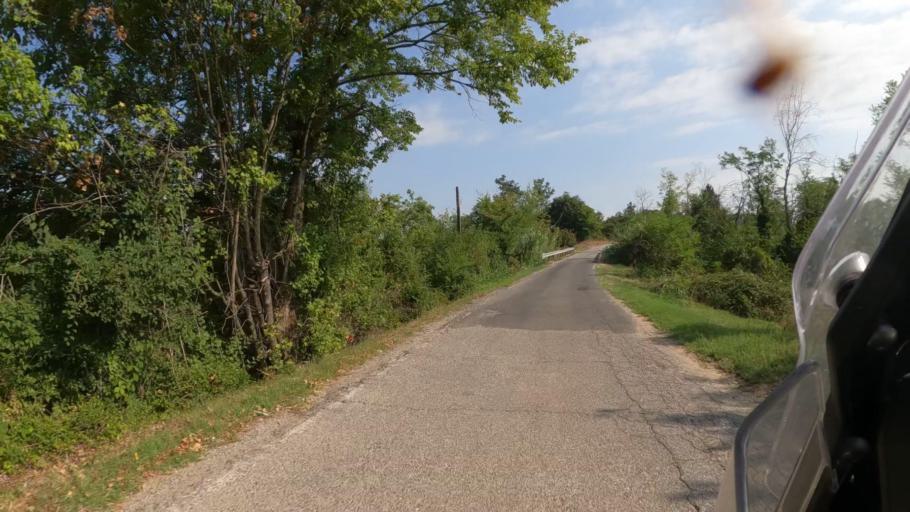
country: IT
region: Piedmont
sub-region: Provincia di Alessandria
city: Altavilla Monferrato
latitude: 44.9651
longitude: 8.3826
